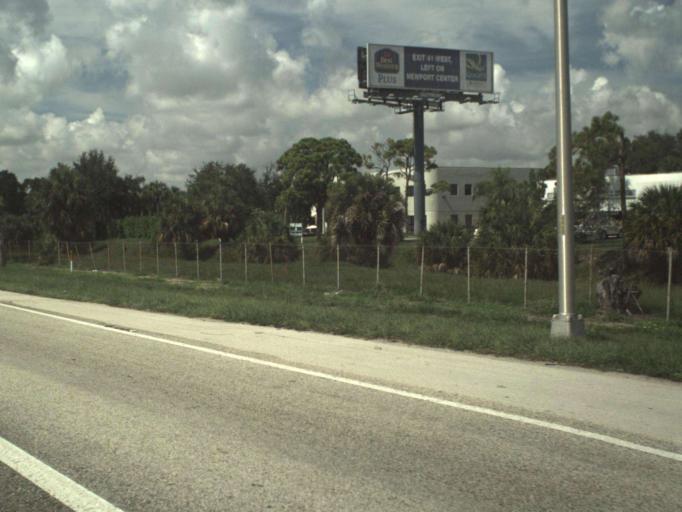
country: US
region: Florida
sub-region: Broward County
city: Deerfield Beach
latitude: 26.3248
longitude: -80.1169
